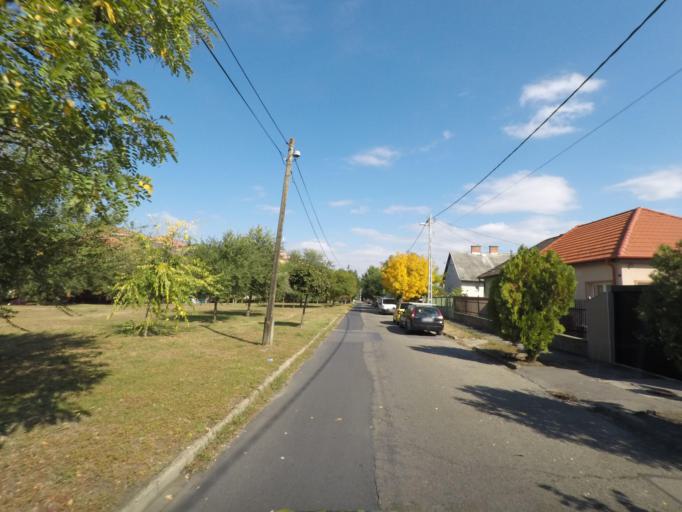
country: HU
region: Budapest
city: Budapest XX. keruelet
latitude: 47.4225
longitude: 19.1103
